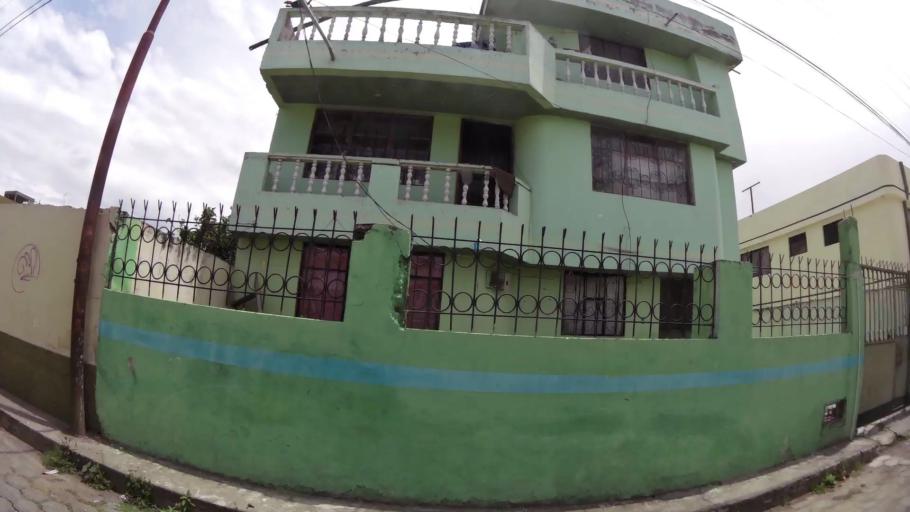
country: EC
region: Cotopaxi
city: San Miguel de Salcedo
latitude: -1.0464
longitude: -78.5873
